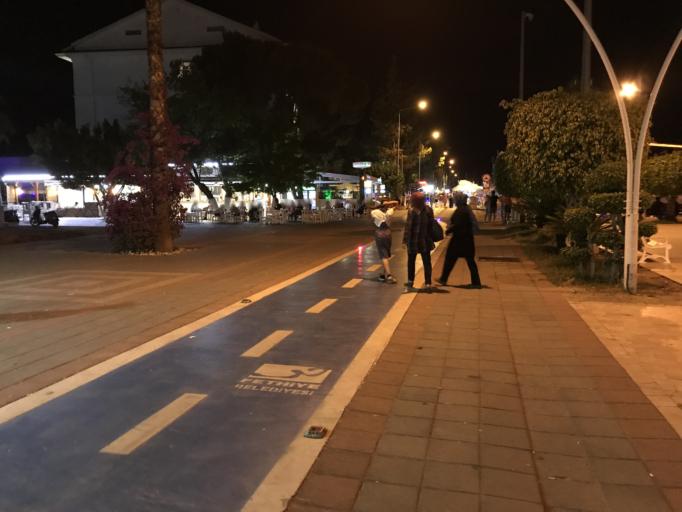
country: TR
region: Mugla
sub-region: Fethiye
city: Fethiye
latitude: 36.6231
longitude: 29.1126
